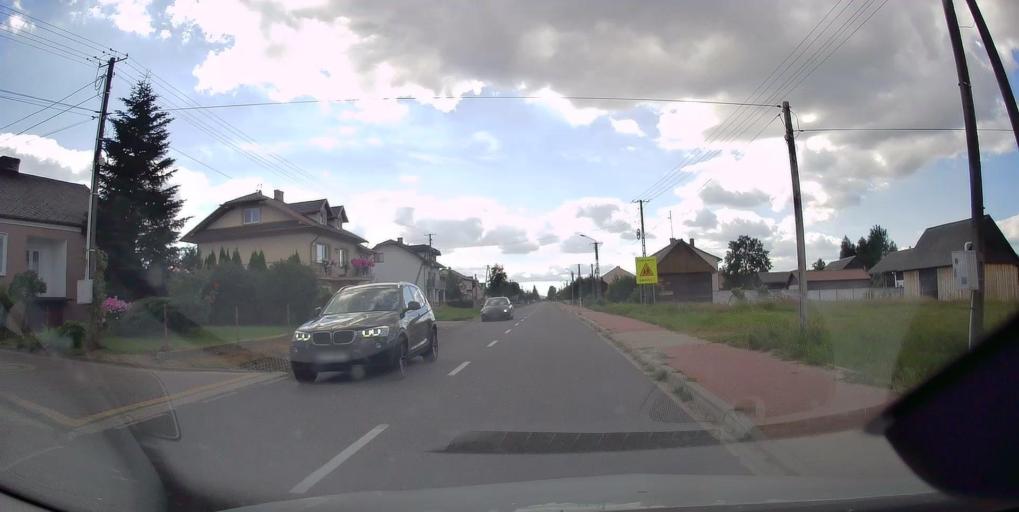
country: PL
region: Swietokrzyskie
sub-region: Powiat kielecki
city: Nowa Slupia
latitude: 50.8929
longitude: 21.0312
